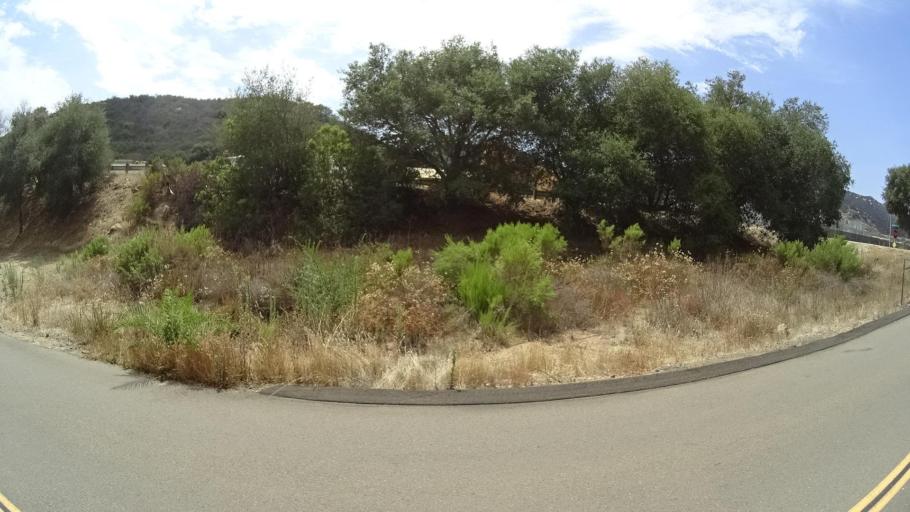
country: US
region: California
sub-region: San Diego County
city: Escondido
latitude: 33.1706
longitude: -117.1061
